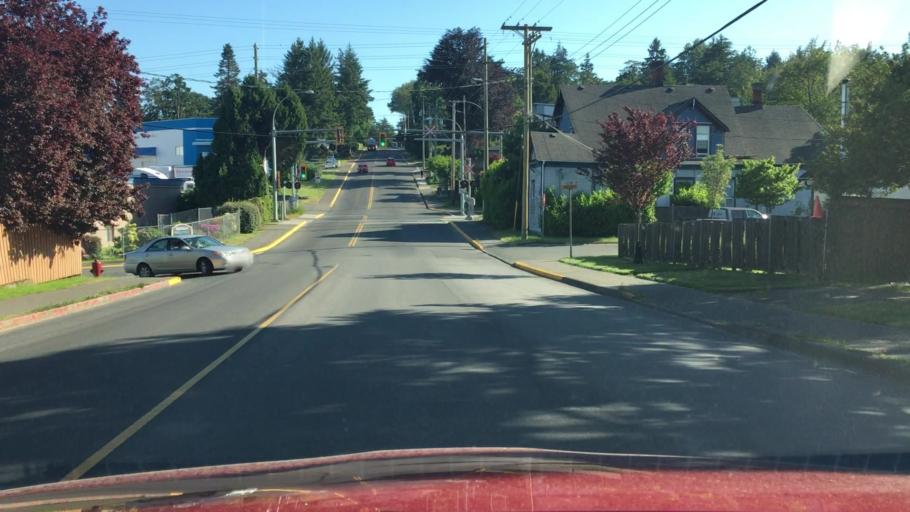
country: CA
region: British Columbia
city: Victoria
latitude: 48.4376
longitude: -123.4024
